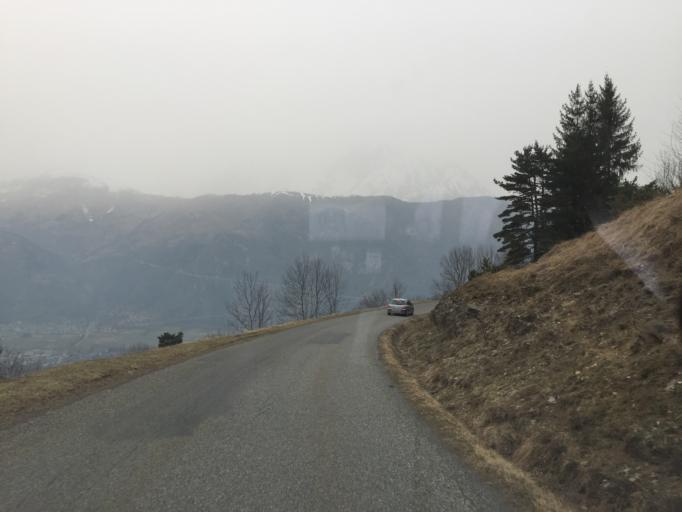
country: FR
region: Midi-Pyrenees
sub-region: Departement des Hautes-Pyrenees
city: Saint-Lary-Soulan
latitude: 42.8160
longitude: 0.3532
